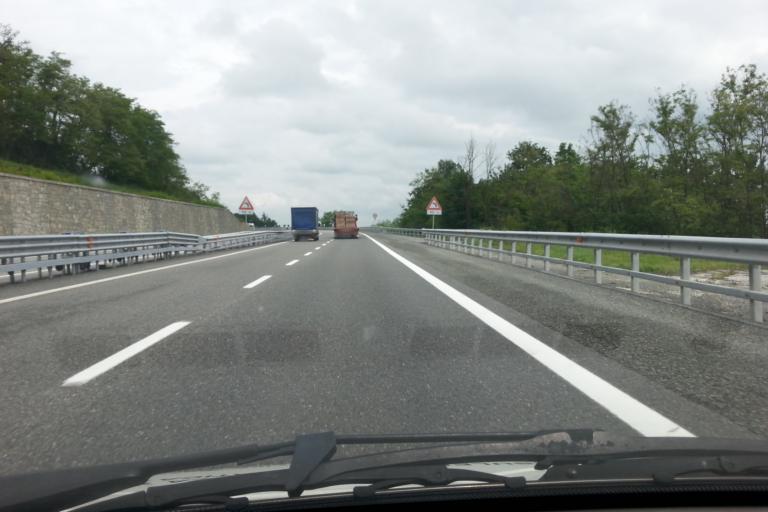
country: IT
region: Piedmont
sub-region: Provincia di Cuneo
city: Bastia Mondovi
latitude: 44.4212
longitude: 7.8893
